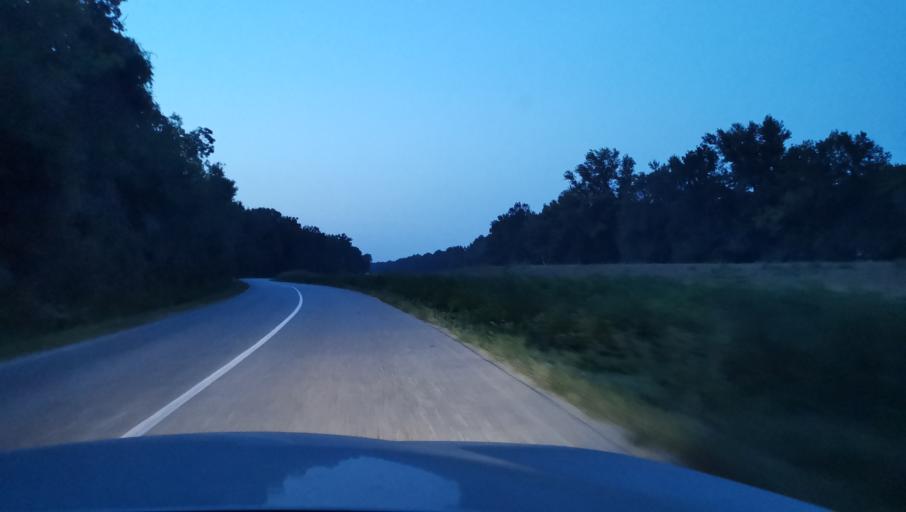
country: RS
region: Central Serbia
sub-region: Belgrade
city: Obrenovac
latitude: 44.6882
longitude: 20.1957
